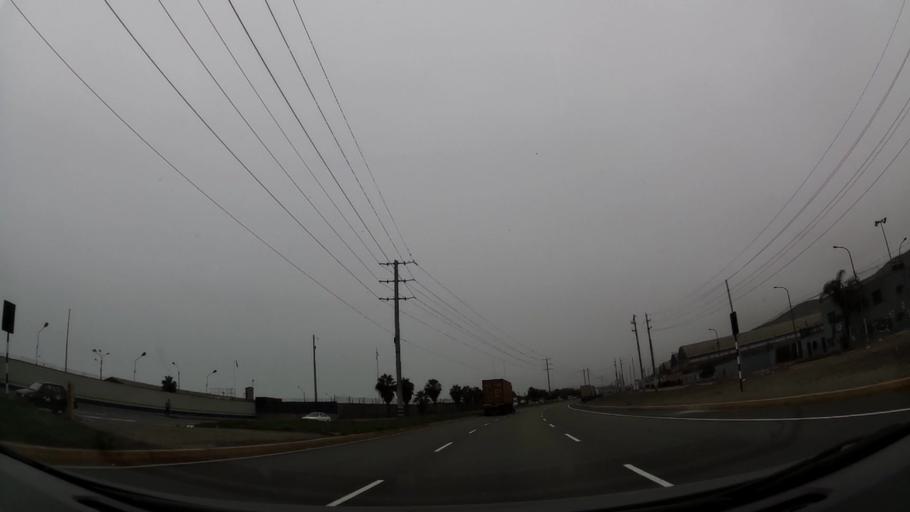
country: PE
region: Lima
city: Ventanilla
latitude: -11.9491
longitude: -77.1316
